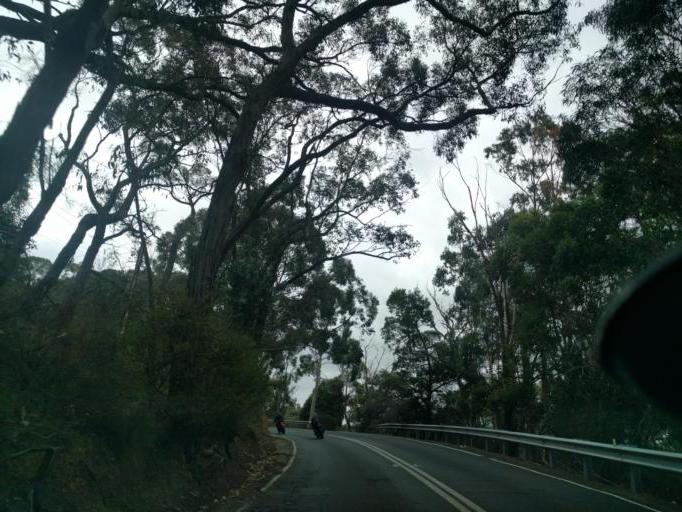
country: AU
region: South Australia
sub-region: Adelaide Hills
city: Stirling
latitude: -35.0256
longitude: 138.7599
